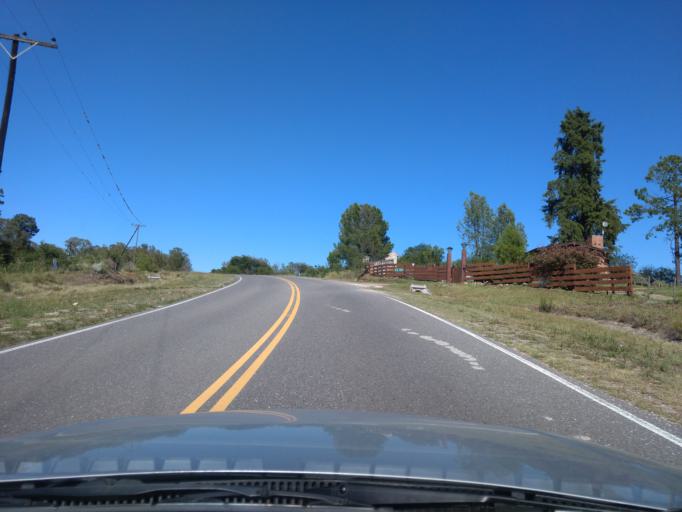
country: AR
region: Cordoba
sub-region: Departamento de Calamuchita
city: Villa General Belgrano
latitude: -31.9633
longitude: -64.6508
